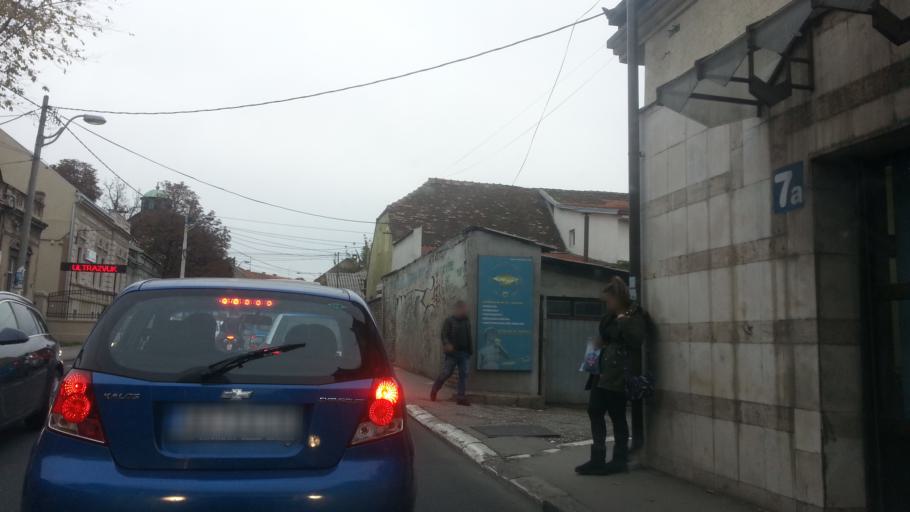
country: RS
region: Central Serbia
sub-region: Belgrade
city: Zemun
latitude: 44.8403
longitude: 20.4038
